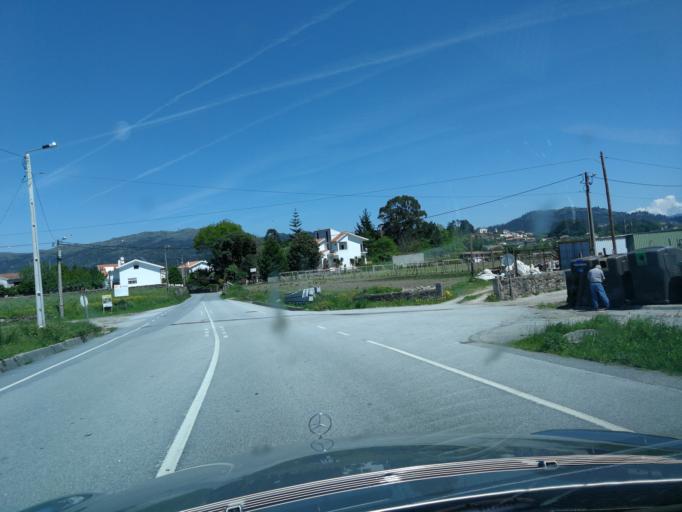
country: PT
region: Viana do Castelo
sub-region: Viana do Castelo
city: Meadela
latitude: 41.7194
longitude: -8.7977
